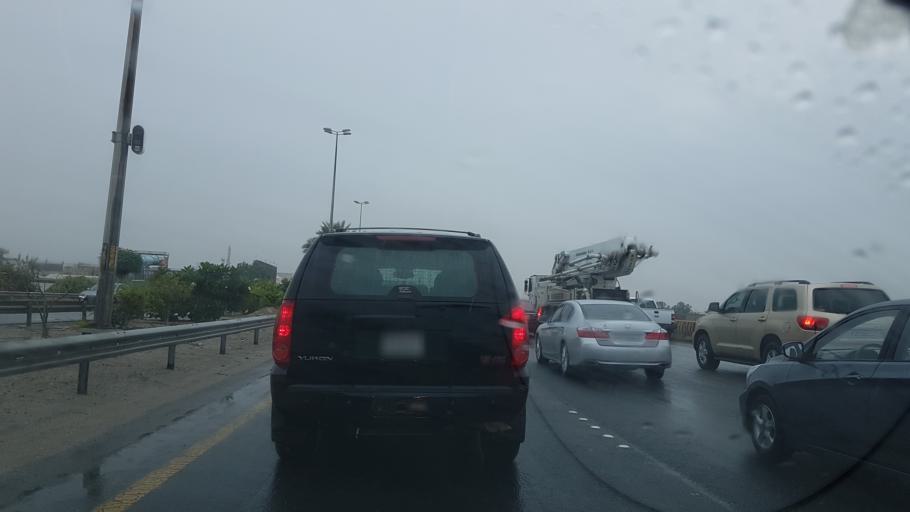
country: BH
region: Manama
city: Jidd Hafs
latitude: 26.1973
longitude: 50.5083
